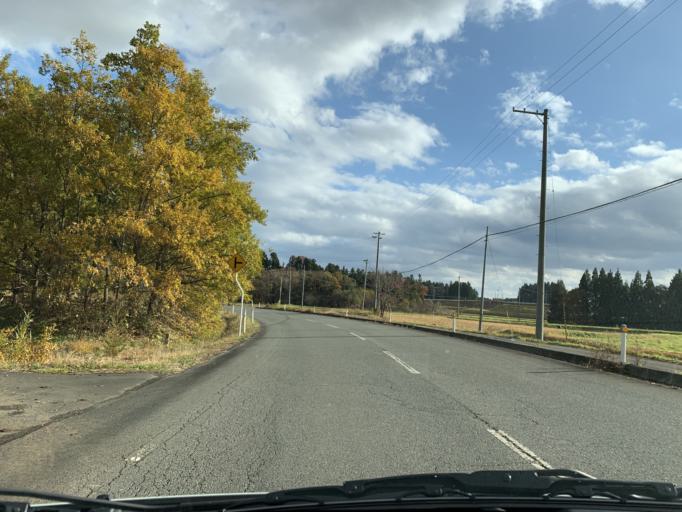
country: JP
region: Iwate
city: Mizusawa
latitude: 39.1125
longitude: 141.0188
